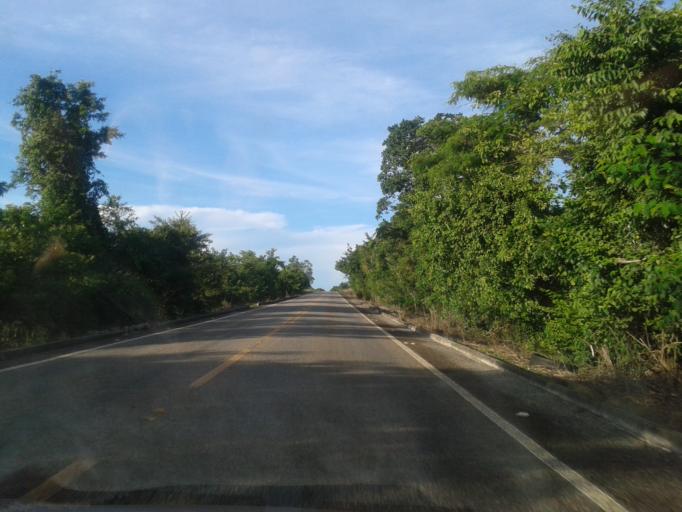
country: BR
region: Goias
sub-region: Sao Miguel Do Araguaia
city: Sao Miguel do Araguaia
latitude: -13.5455
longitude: -50.3080
